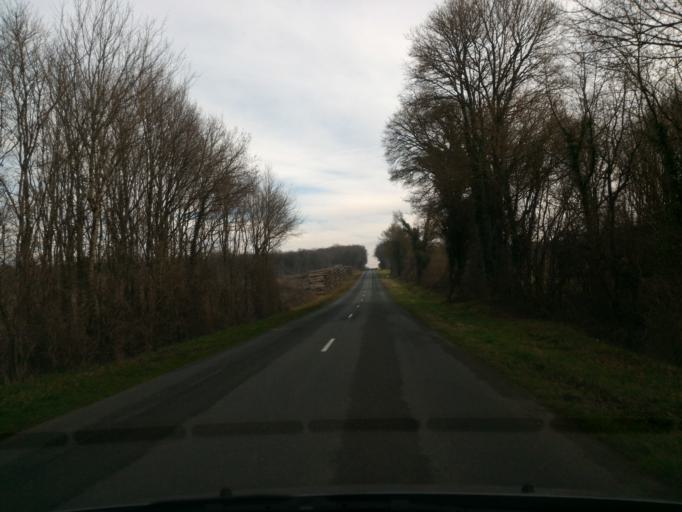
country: FR
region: Poitou-Charentes
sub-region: Departement de la Charente
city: Aigre
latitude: 45.9210
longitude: 0.0541
